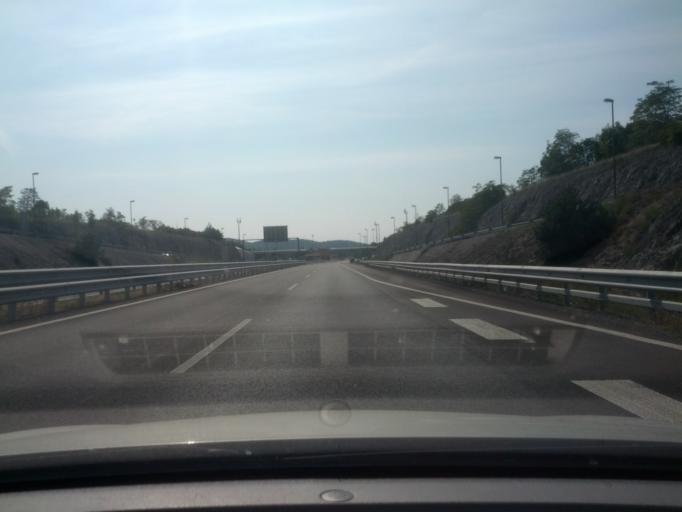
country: SI
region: Sezana
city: Sezana
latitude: 45.7025
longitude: 13.8413
